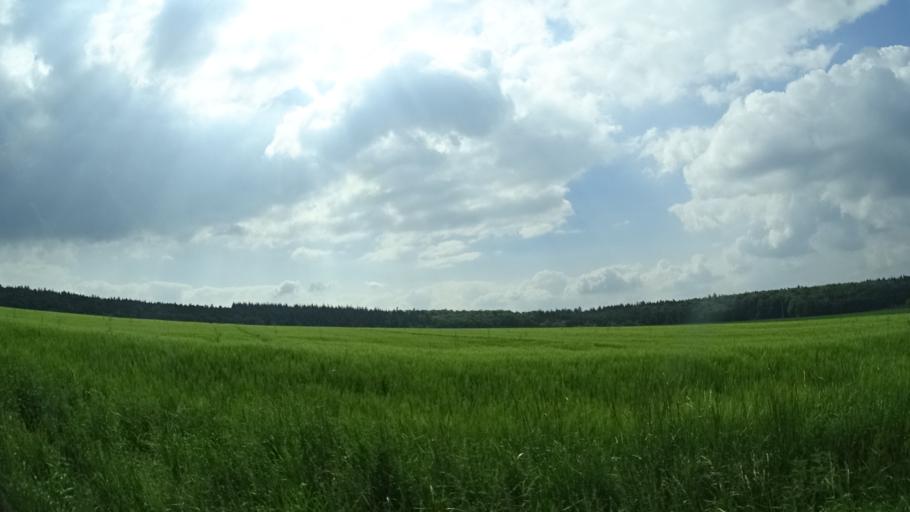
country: DE
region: Bavaria
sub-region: Regierungsbezirk Unterfranken
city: Wartmannsroth
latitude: 50.1748
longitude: 9.8051
